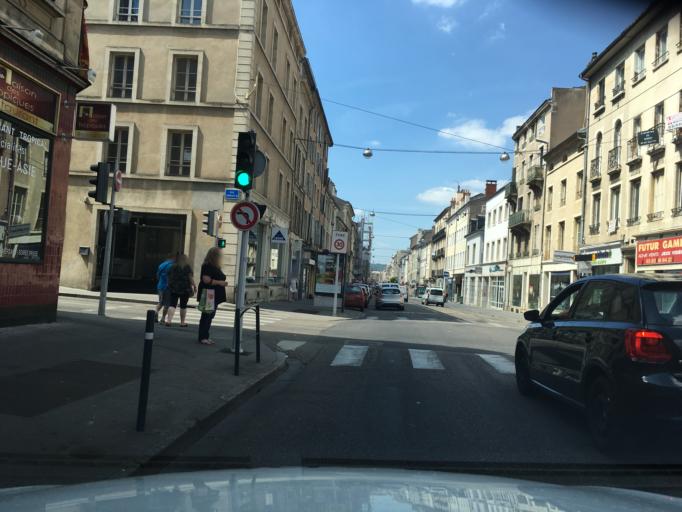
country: FR
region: Lorraine
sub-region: Departement de Meurthe-et-Moselle
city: Nancy
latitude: 48.6867
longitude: 6.1854
